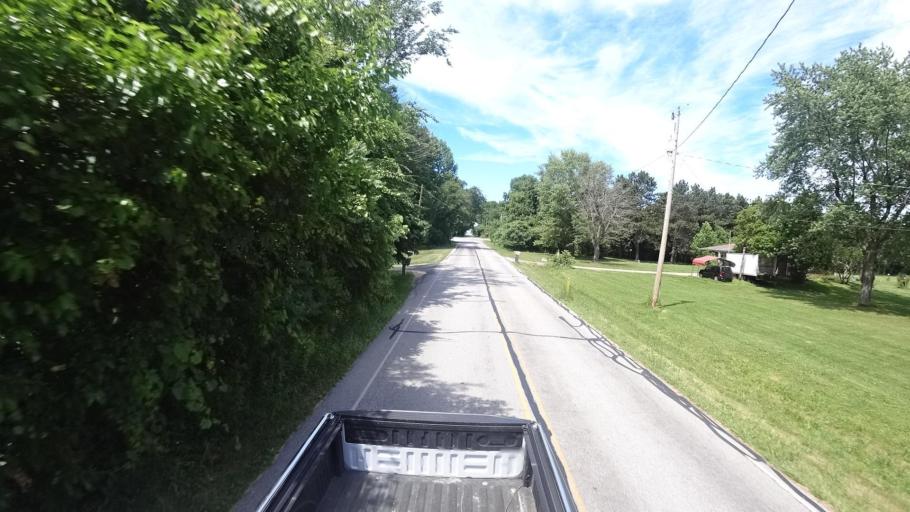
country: US
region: Indiana
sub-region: Porter County
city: Porter
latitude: 41.6264
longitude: -87.0770
